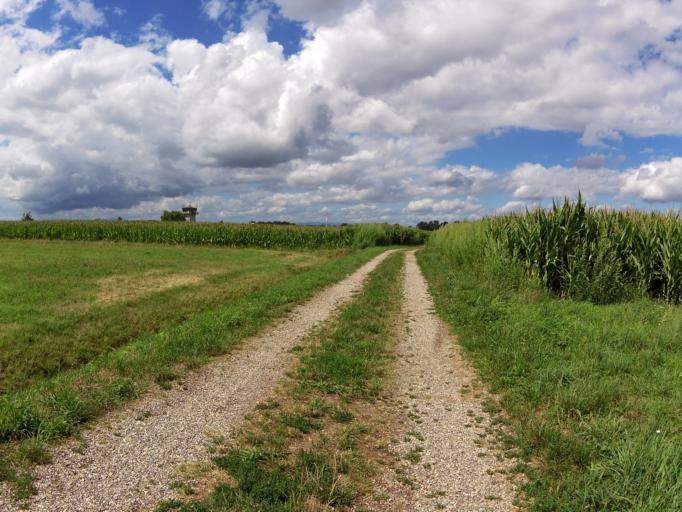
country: DE
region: Baden-Wuerttemberg
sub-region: Freiburg Region
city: Lahr
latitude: 48.3646
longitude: 7.8311
